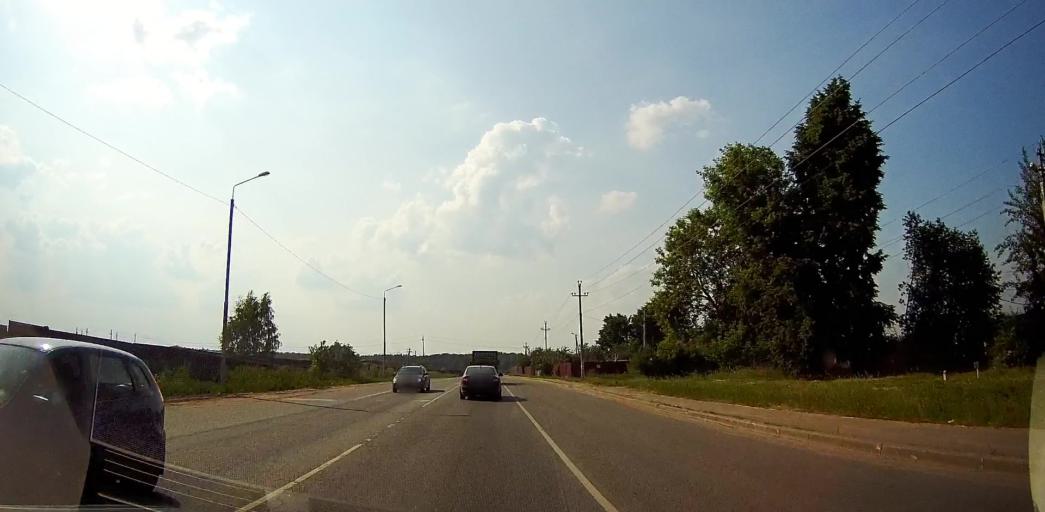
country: RU
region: Moskovskaya
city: Zhitnevo
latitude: 55.3797
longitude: 37.8781
